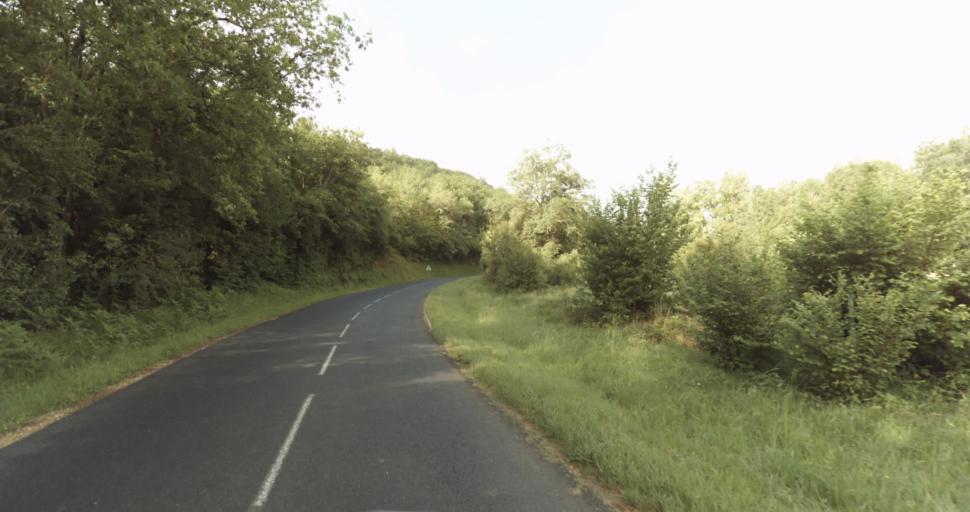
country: FR
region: Aquitaine
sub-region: Departement de la Dordogne
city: Vergt
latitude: 44.9363
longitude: 0.7794
